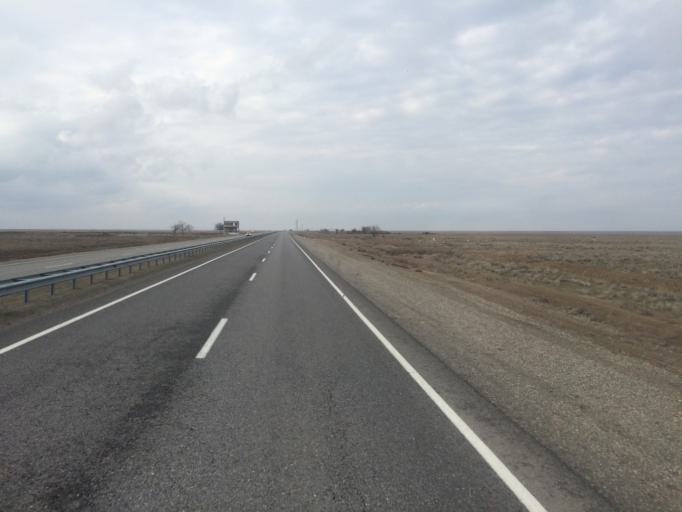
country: KZ
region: Ongtustik Qazaqstan
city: Turkestan
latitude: 43.5249
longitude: 67.7955
